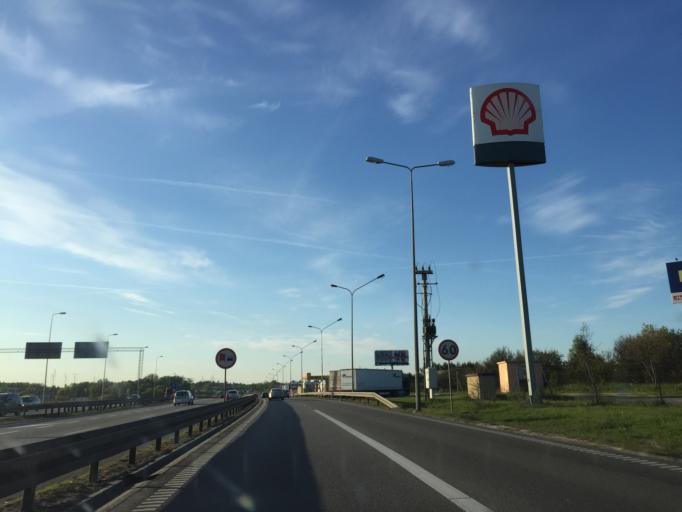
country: PL
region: Pomeranian Voivodeship
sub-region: Powiat gdanski
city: Kowale
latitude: 54.3651
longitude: 18.5197
